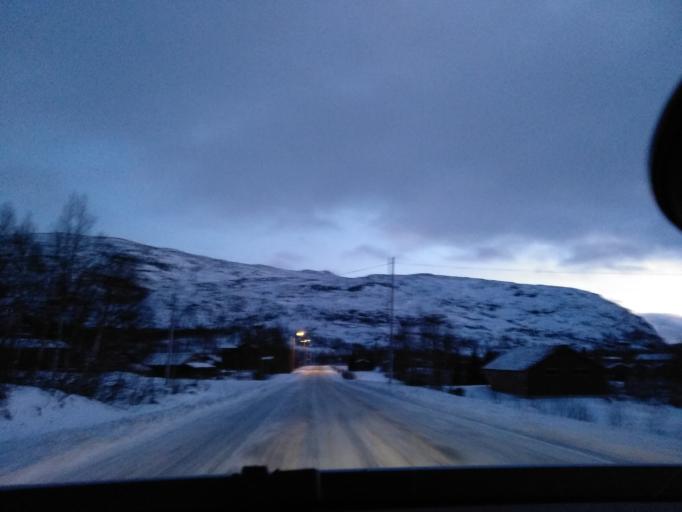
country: NO
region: Vest-Agder
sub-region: Sirdal
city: Tonstad
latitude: 59.0161
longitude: 6.9372
